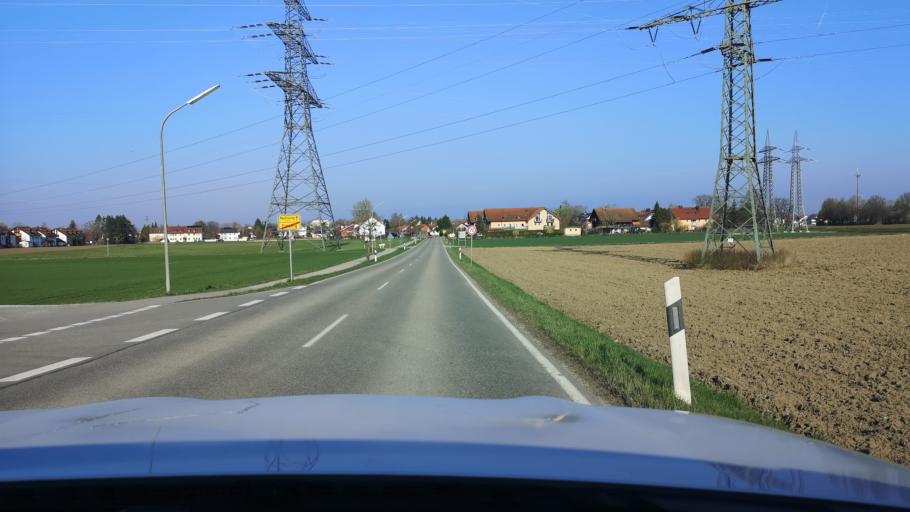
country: DE
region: Bavaria
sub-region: Upper Bavaria
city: Finsing
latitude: 48.2180
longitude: 11.8126
